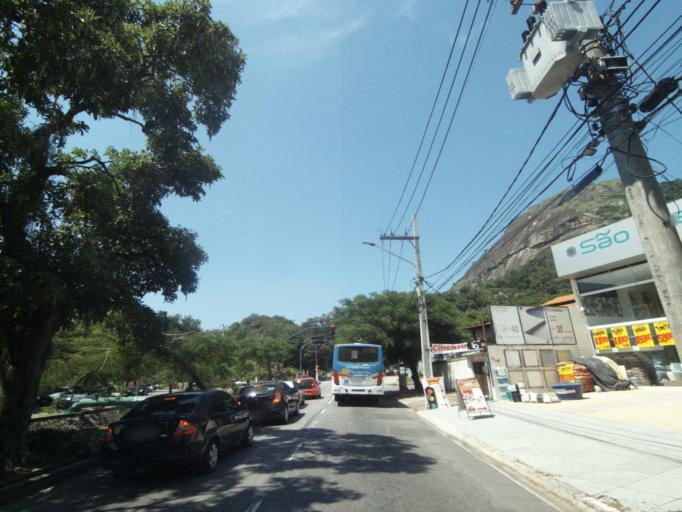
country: BR
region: Rio de Janeiro
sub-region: Niteroi
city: Niteroi
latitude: -22.9141
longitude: -43.0844
